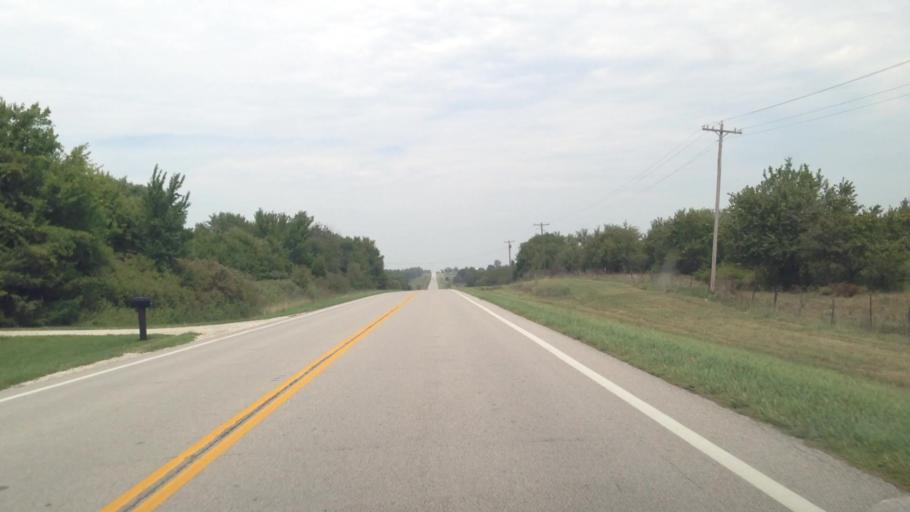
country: US
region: Kansas
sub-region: Neosho County
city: Erie
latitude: 37.6545
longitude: -95.2516
